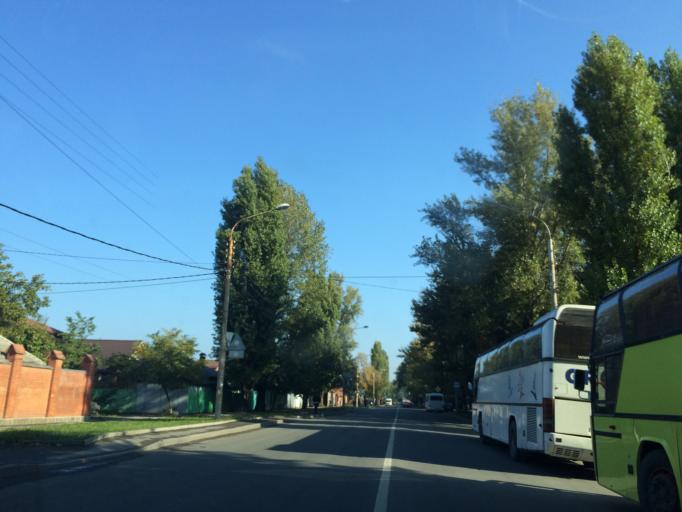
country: RU
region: Rostov
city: Imeni Chkalova
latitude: 47.2691
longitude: 39.7887
